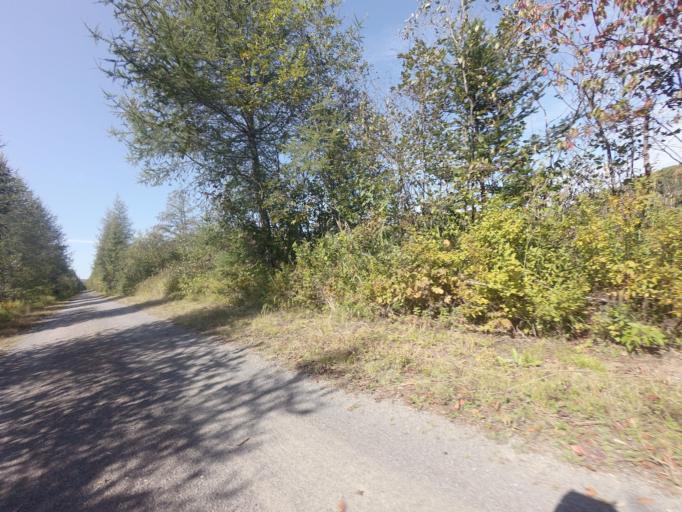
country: CA
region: Quebec
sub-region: Laurentides
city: Sainte-Agathe-des-Monts
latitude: 46.1034
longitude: -74.3739
